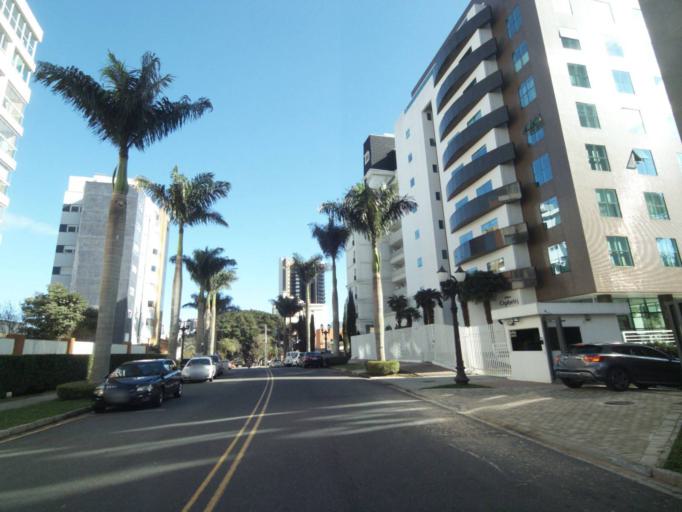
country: BR
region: Parana
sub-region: Curitiba
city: Curitiba
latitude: -25.4114
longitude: -49.2440
